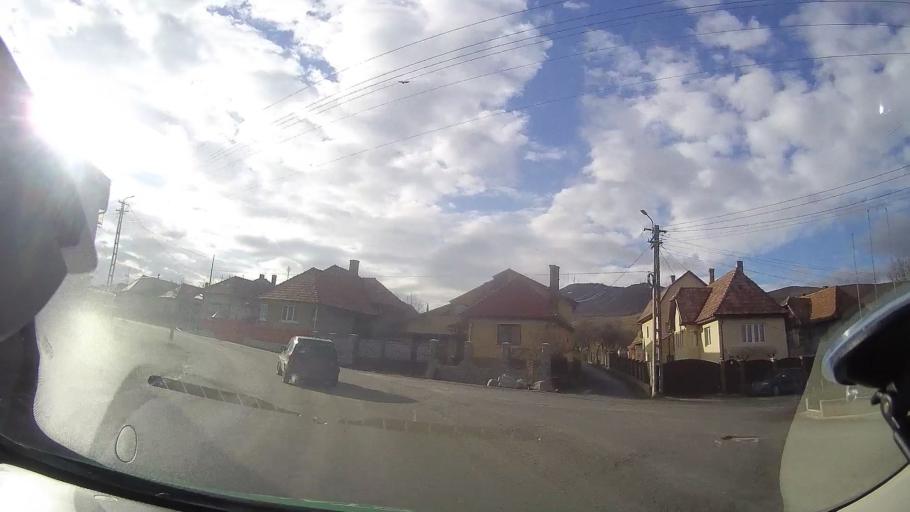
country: RO
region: Cluj
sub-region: Comuna Baisoara
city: Baisoara
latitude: 46.6196
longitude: 23.4521
